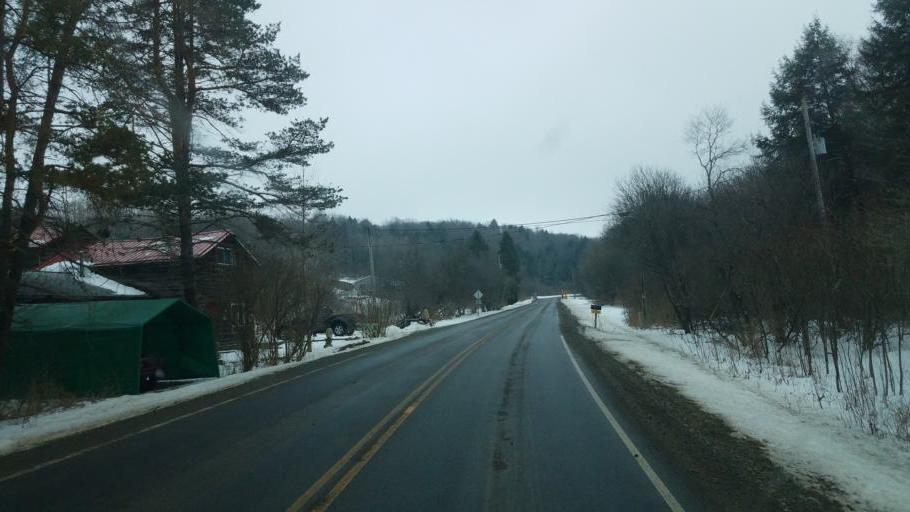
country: US
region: New York
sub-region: Allegany County
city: Andover
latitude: 42.0303
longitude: -77.7504
